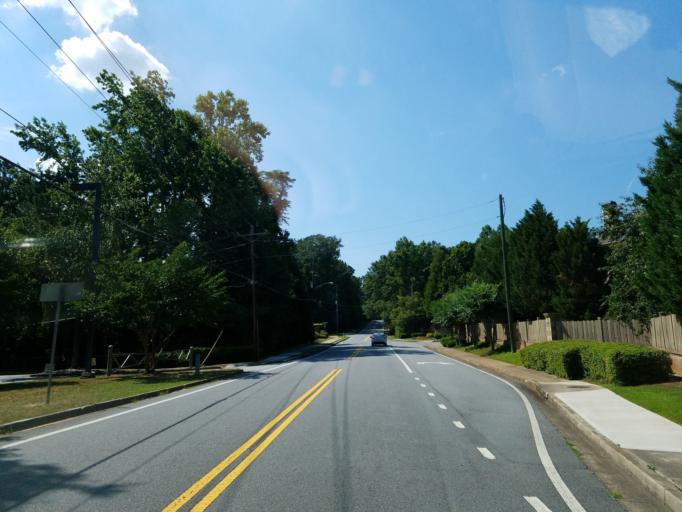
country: US
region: Georgia
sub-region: Fulton County
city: Roswell
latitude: 34.0507
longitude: -84.4342
